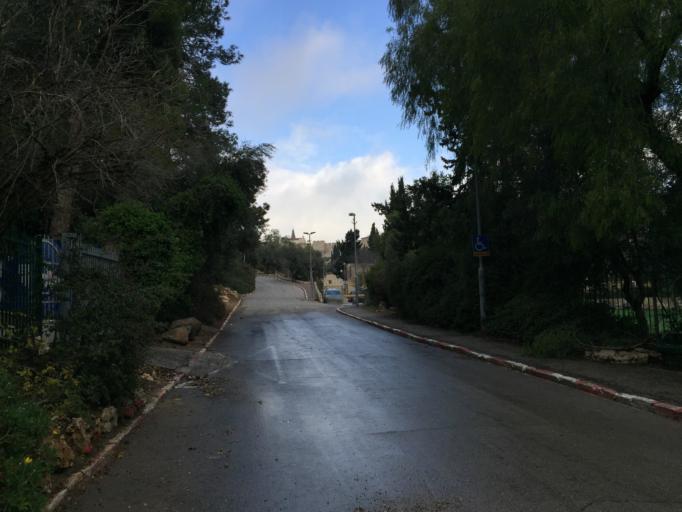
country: PS
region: West Bank
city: Old City
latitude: 31.7737
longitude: 35.2259
